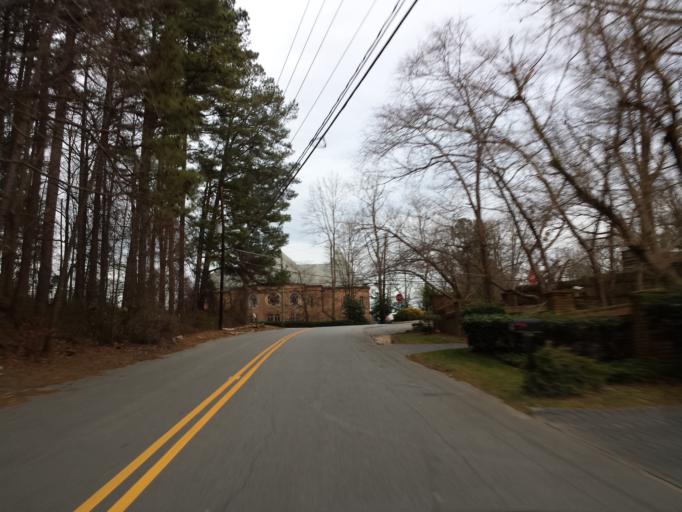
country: US
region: Georgia
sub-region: Cobb County
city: Vinings
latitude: 33.8778
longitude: -84.4129
